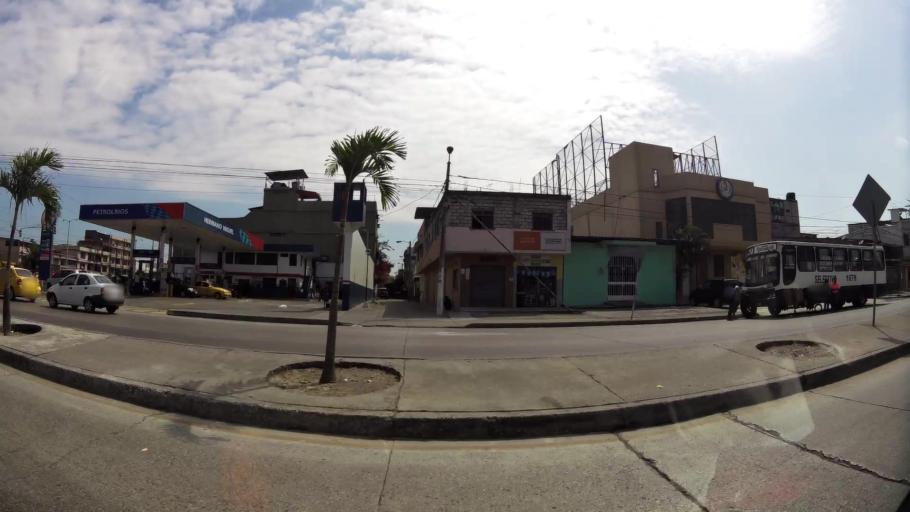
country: EC
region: Guayas
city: Guayaquil
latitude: -2.2513
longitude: -79.8939
